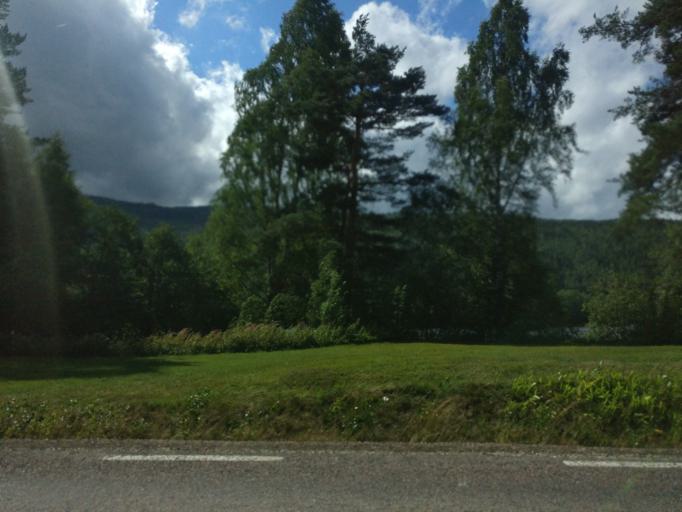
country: SE
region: Vaermland
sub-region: Hagfors Kommun
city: Ekshaerad
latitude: 60.3684
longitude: 13.3062
